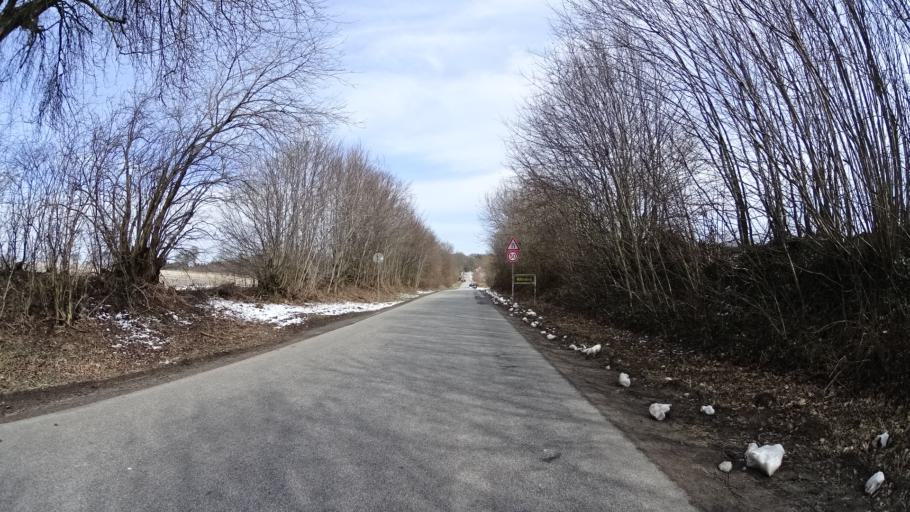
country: DE
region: Schleswig-Holstein
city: Stolpe
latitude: 54.1357
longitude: 10.2238
